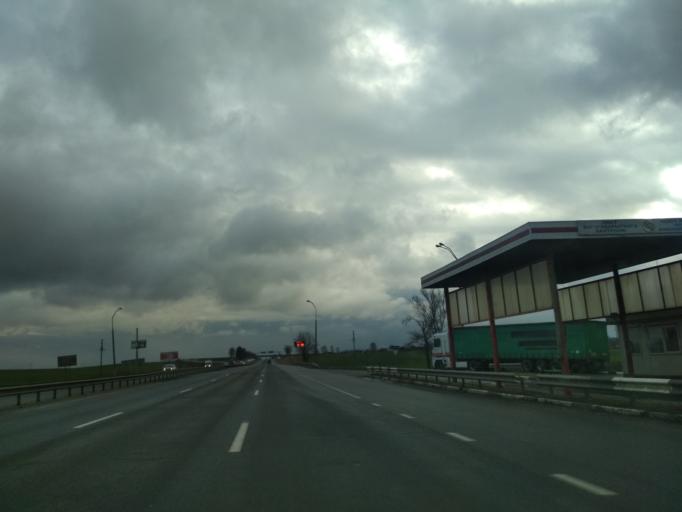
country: BY
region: Minsk
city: Pryvol'ny
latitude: 53.7977
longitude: 27.8080
